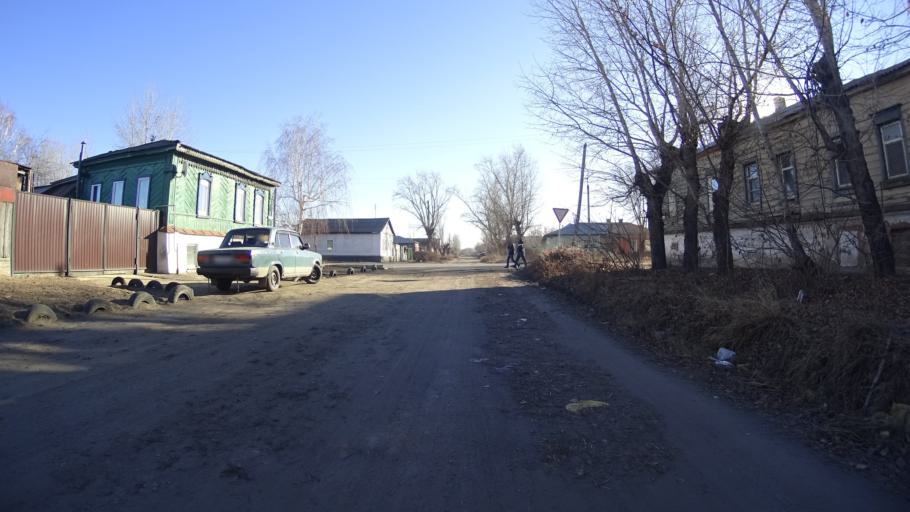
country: RU
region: Chelyabinsk
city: Troitsk
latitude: 54.0863
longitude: 61.5686
